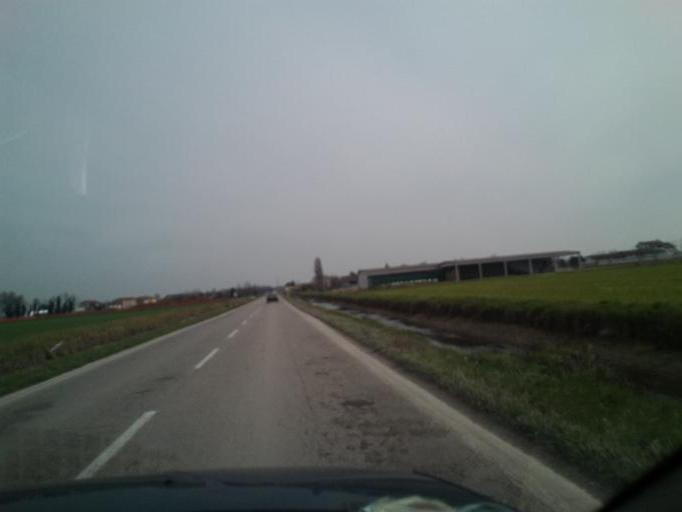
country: IT
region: Lombardy
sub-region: Provincia di Mantova
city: Roverbella
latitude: 45.2589
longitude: 10.7469
